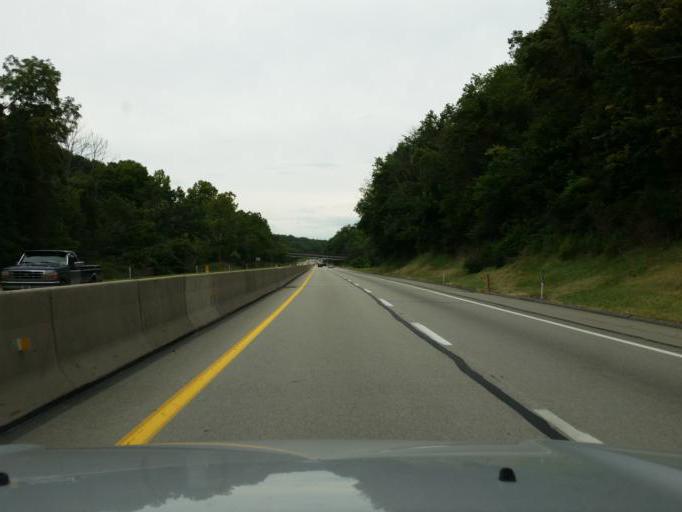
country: US
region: Pennsylvania
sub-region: Westmoreland County
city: Level Green
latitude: 40.3892
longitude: -79.6852
